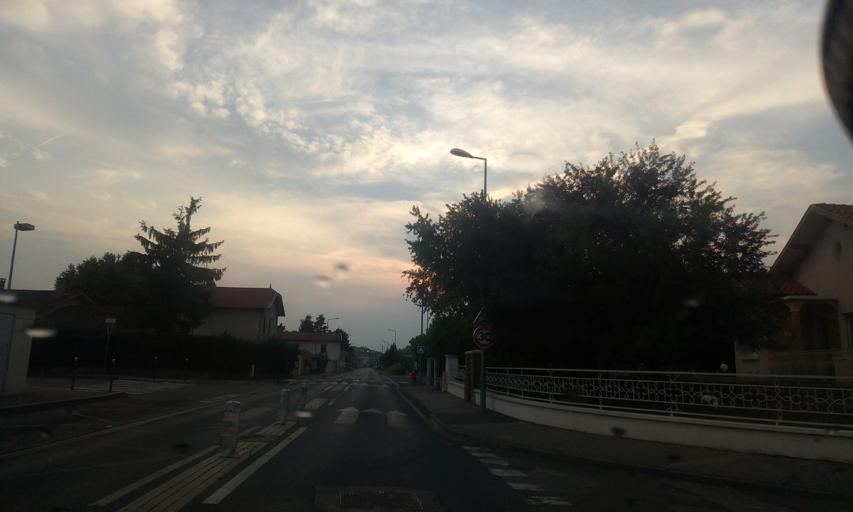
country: FR
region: Rhone-Alpes
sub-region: Departement du Rhone
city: Chassieu
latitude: 45.7358
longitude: 4.9786
